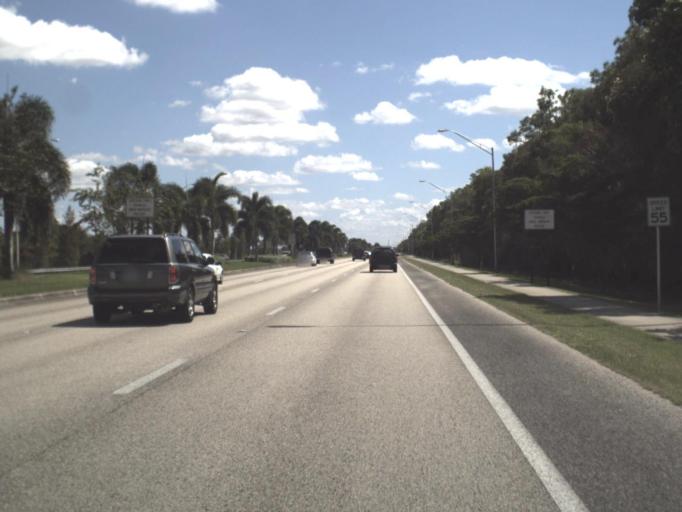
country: US
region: Florida
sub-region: Collier County
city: Lely Resort
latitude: 26.0730
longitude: -81.7147
